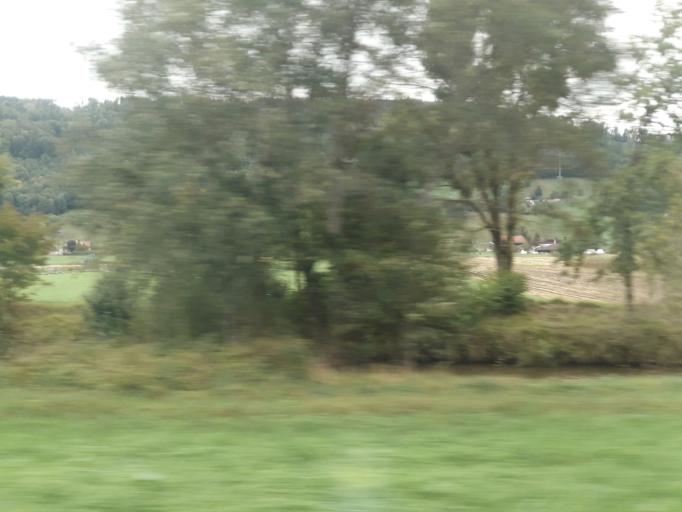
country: CH
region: Bern
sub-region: Bern-Mittelland District
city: Toffen
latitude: 46.8640
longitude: 7.4956
